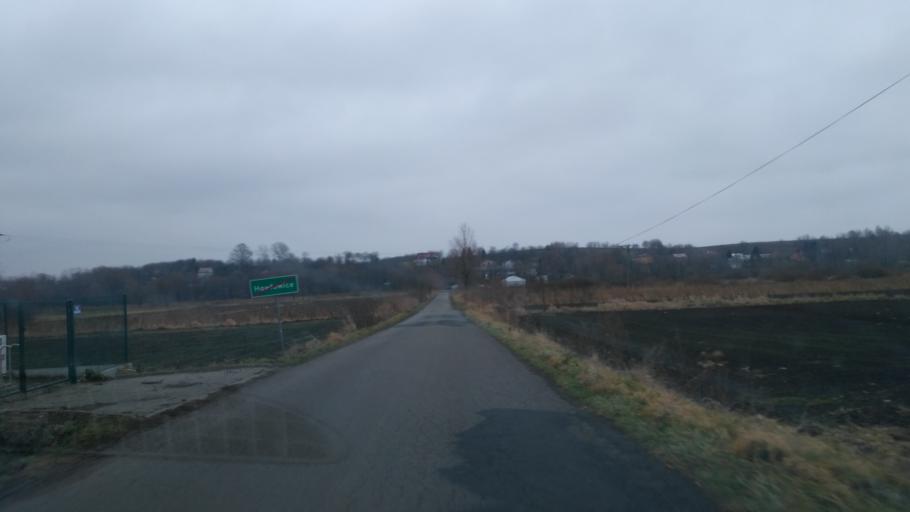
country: PL
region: Subcarpathian Voivodeship
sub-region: Powiat przeworski
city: Zarzecze
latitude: 49.9374
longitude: 22.5613
